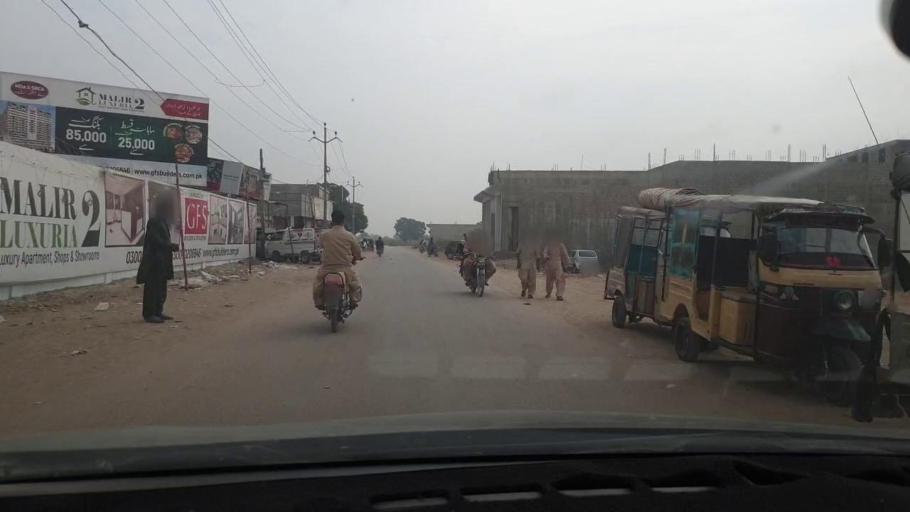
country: PK
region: Sindh
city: Malir Cantonment
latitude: 24.9192
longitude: 67.2582
